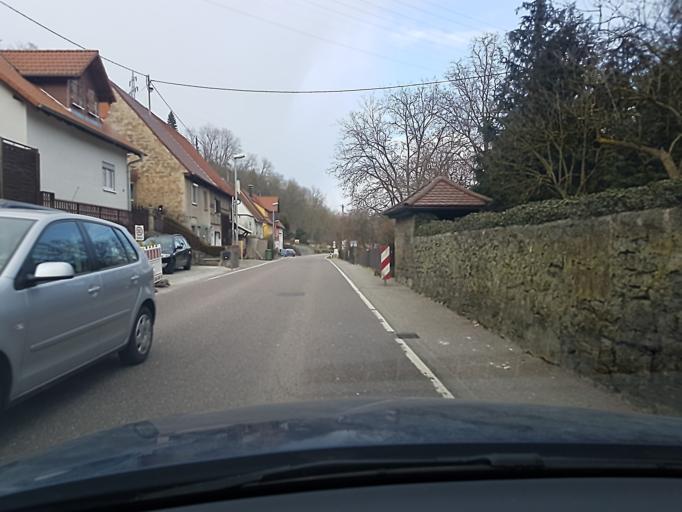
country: DE
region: Baden-Wuerttemberg
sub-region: Regierungsbezirk Stuttgart
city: Eberdingen
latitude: 48.8967
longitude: 8.9715
